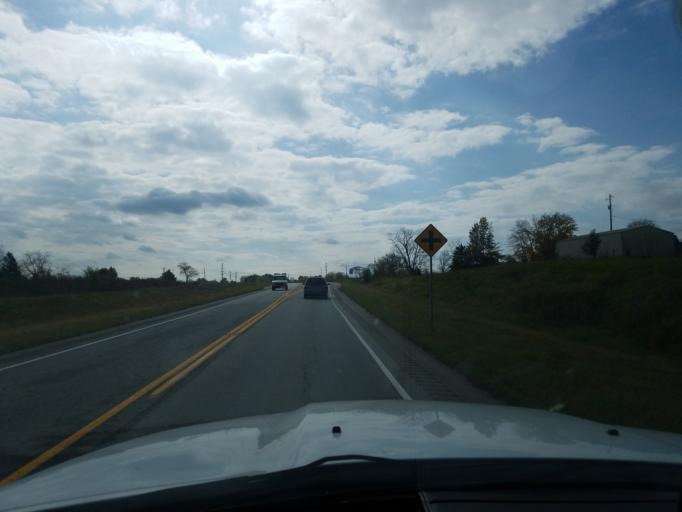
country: US
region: Kentucky
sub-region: Nelson County
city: Bardstown
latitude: 37.9016
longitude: -85.4733
